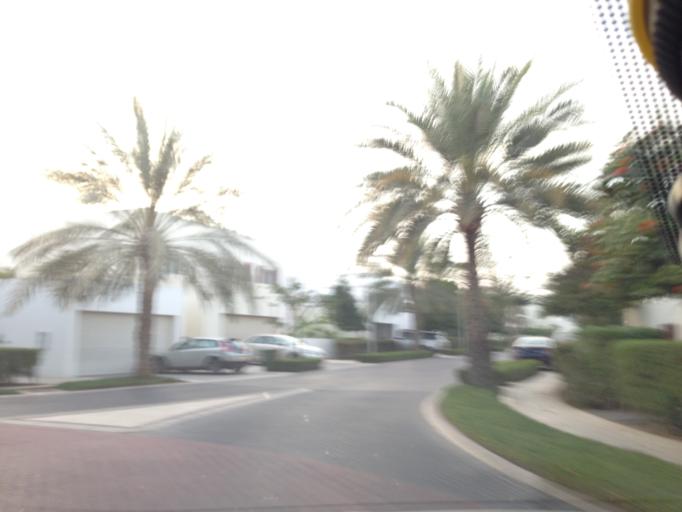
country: OM
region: Muhafazat Masqat
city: As Sib al Jadidah
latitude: 23.6247
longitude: 58.2725
